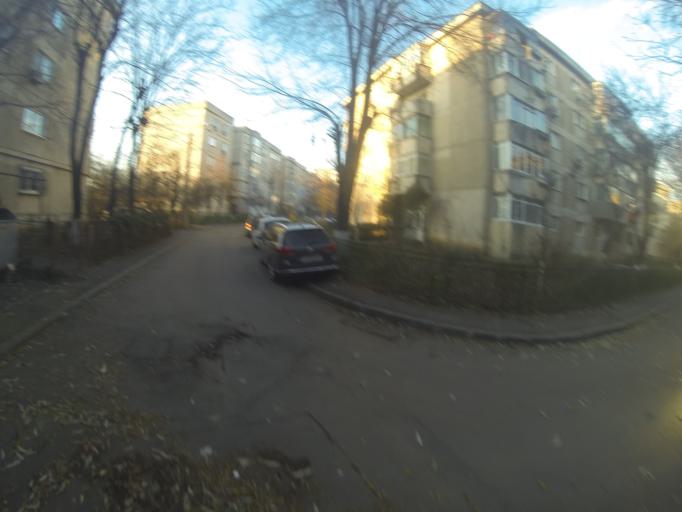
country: RO
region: Bucuresti
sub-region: Municipiul Bucuresti
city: Bucuresti
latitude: 44.4087
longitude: 26.0823
